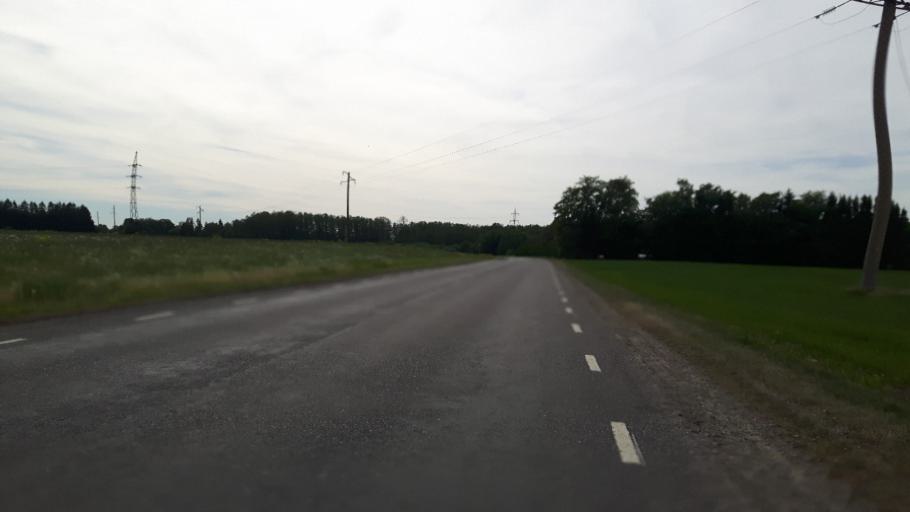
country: EE
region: Harju
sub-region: Maardu linn
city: Maardu
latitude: 59.4258
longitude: 25.0228
